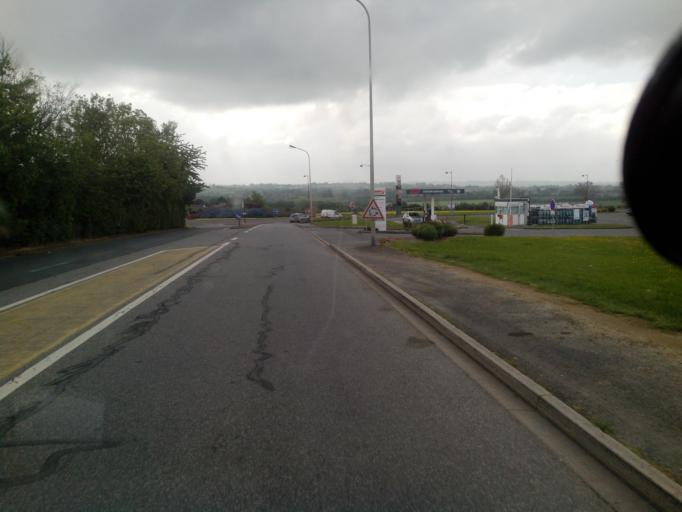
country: FR
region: Lower Normandy
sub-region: Departement du Calvados
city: Villers-Bocage
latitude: 49.0735
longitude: -0.6570
